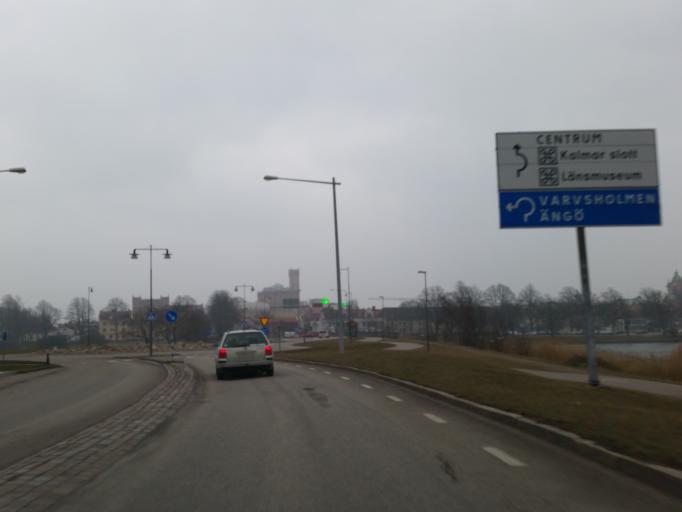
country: SE
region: Kalmar
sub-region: Kalmar Kommun
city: Kalmar
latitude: 56.6690
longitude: 16.3672
